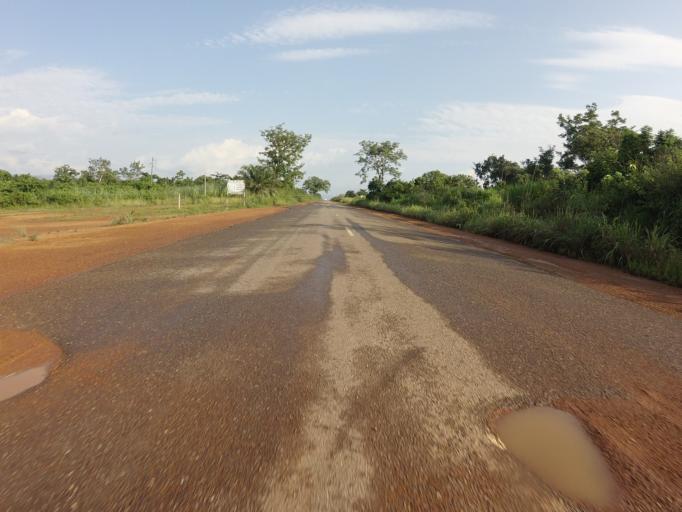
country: GH
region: Volta
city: Hohoe
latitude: 7.0310
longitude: 0.4274
